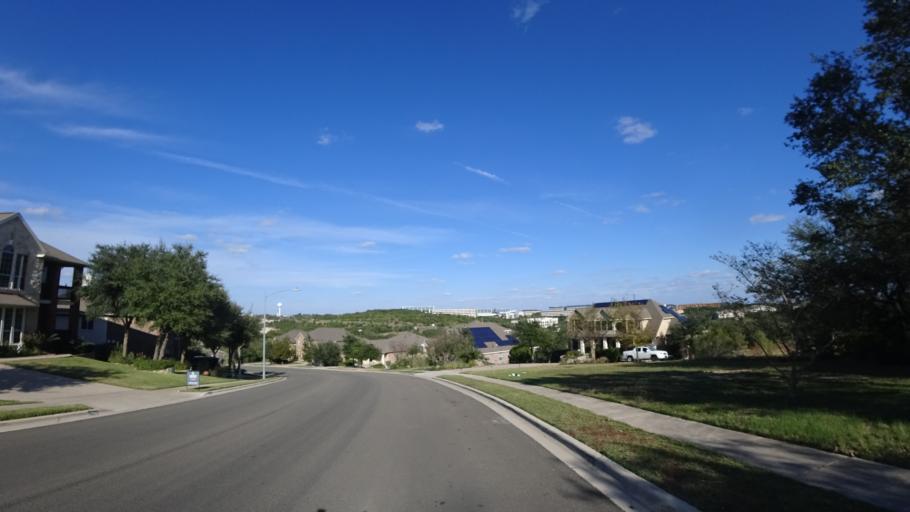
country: US
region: Texas
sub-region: Travis County
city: Barton Creek
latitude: 30.2473
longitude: -97.8706
